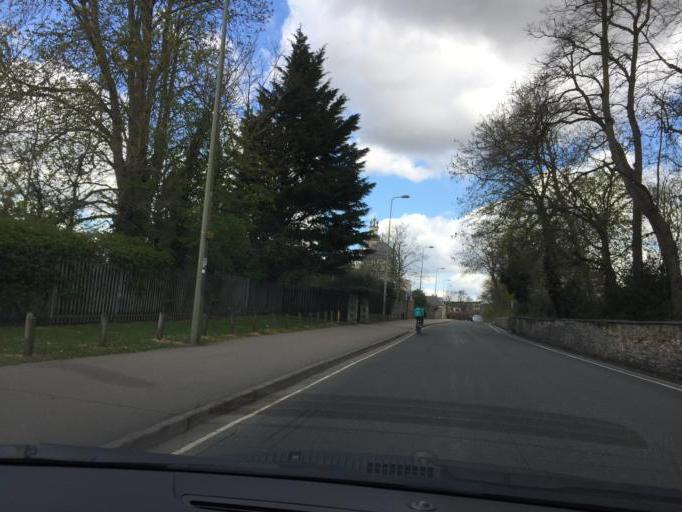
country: GB
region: England
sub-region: Oxfordshire
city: Oxford
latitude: 51.7538
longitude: -1.2361
